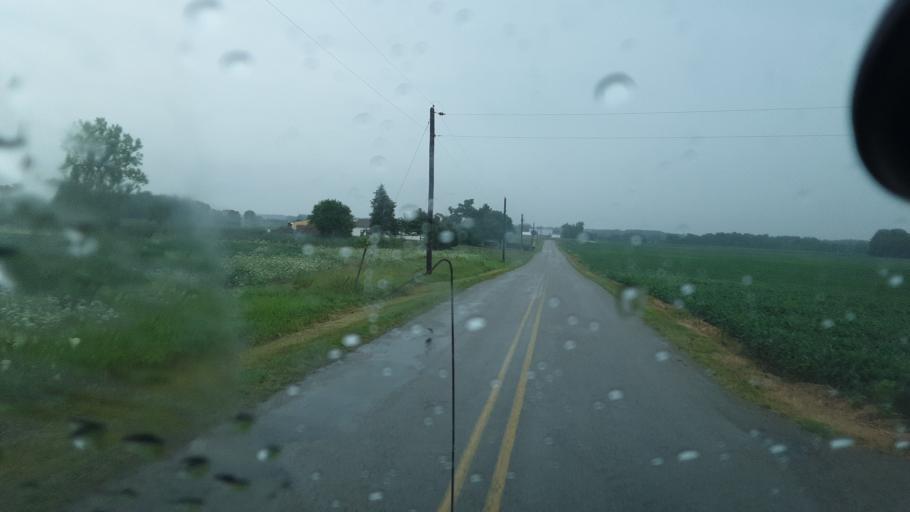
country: US
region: Indiana
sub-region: DeKalb County
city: Butler
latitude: 41.4503
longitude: -84.8136
